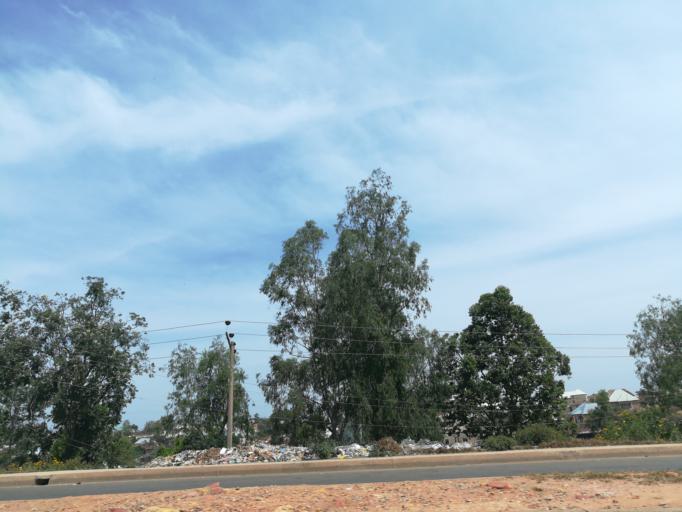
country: NG
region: Plateau
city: Bukuru
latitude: 9.8365
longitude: 8.8663
